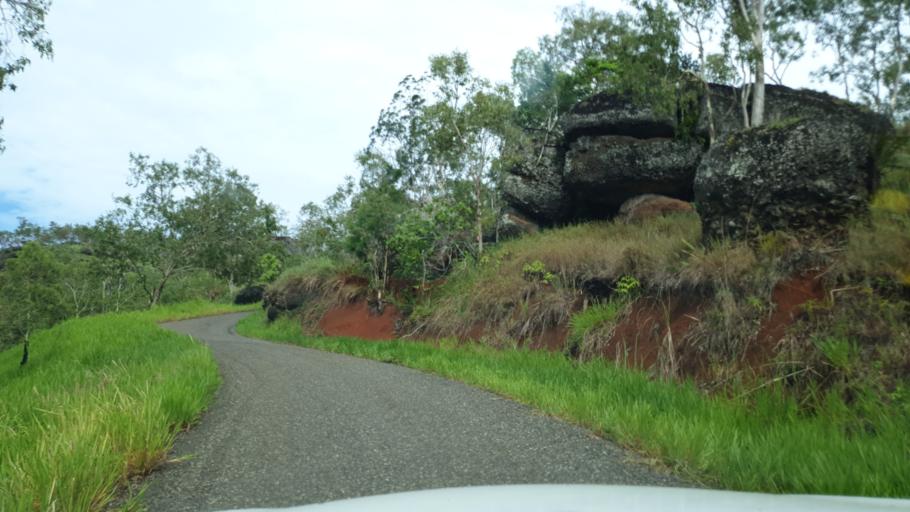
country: PG
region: National Capital
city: Port Moresby
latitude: -9.4355
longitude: 147.3918
